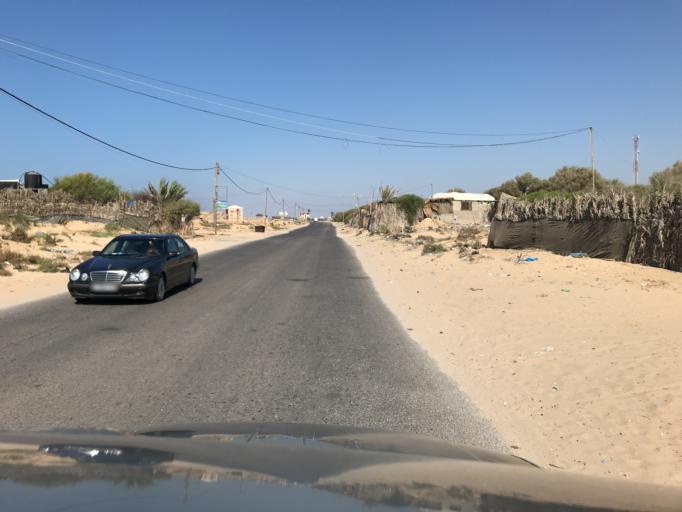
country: PS
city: Wadi as Salqa
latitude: 31.3943
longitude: 34.3017
